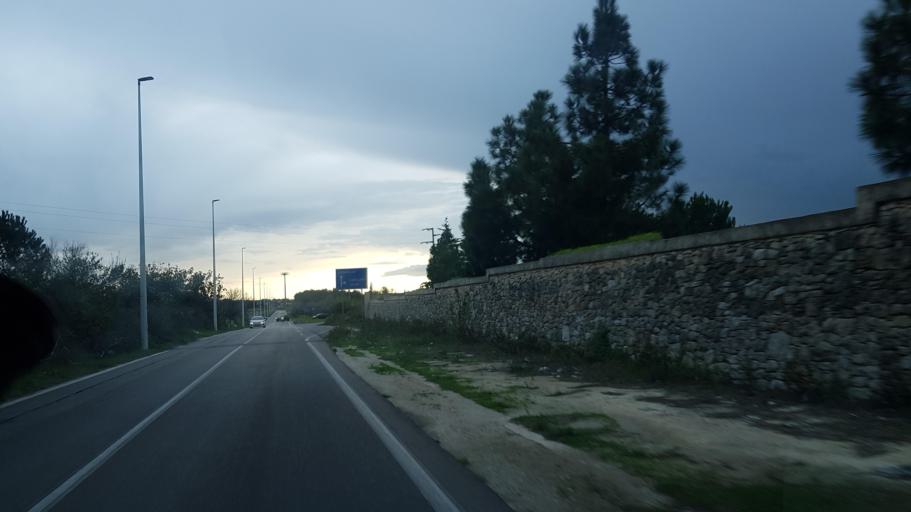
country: IT
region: Apulia
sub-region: Provincia di Lecce
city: Merine
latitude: 40.3216
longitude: 18.2233
